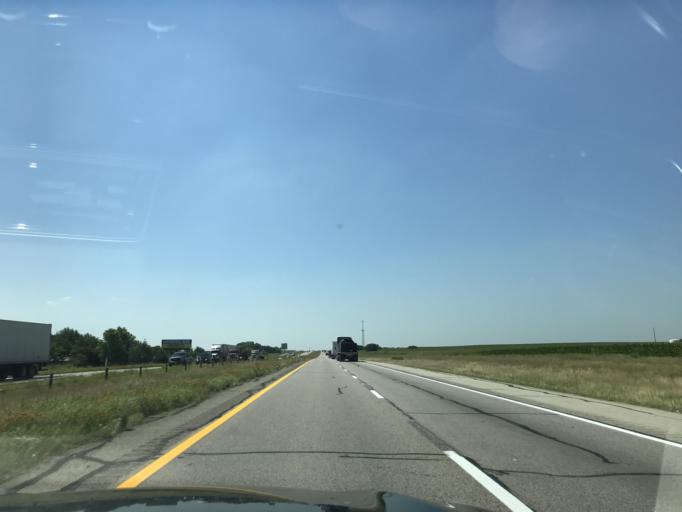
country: US
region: Texas
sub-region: Johnson County
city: Alvarado
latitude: 32.3419
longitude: -97.1928
